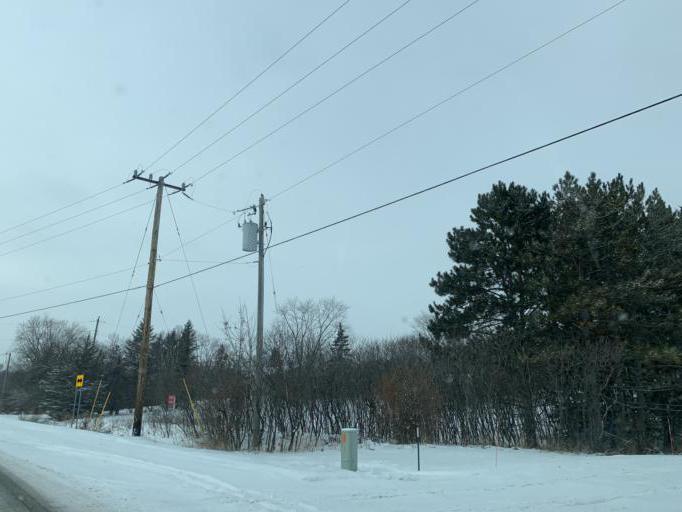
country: US
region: Minnesota
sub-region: Washington County
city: Cottage Grove
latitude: 44.8764
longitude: -92.9094
